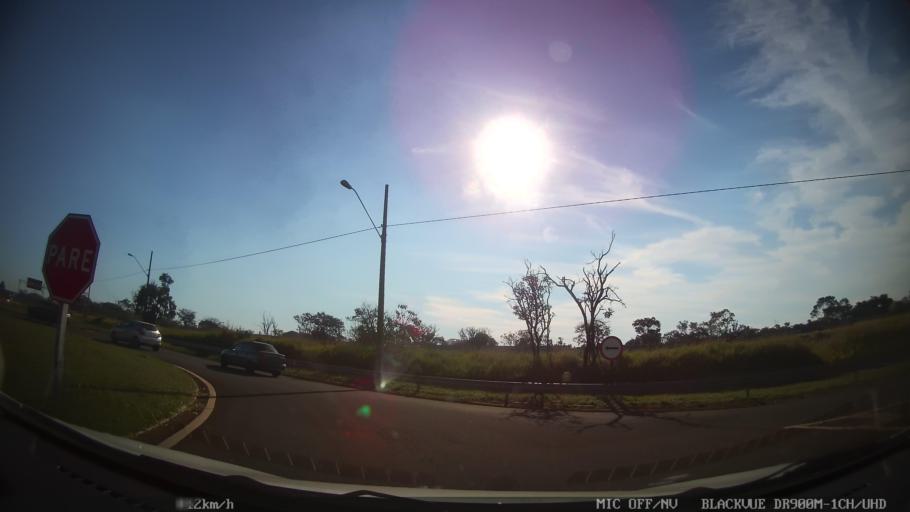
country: BR
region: Sao Paulo
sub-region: Americo Brasiliense
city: Americo Brasiliense
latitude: -21.7619
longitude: -48.1359
